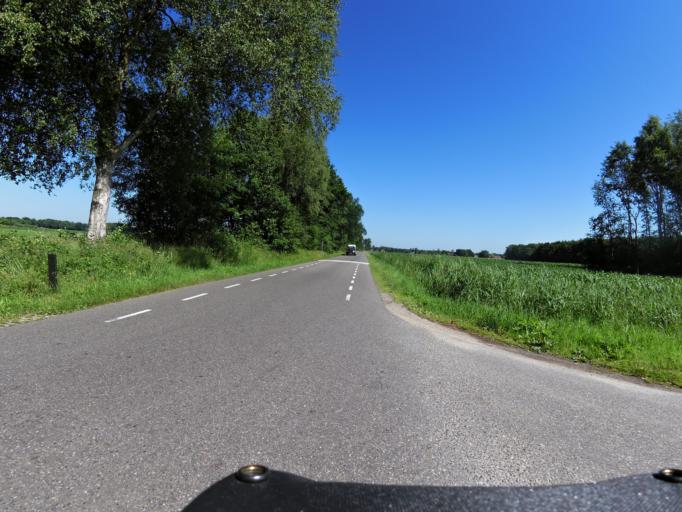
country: NL
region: Overijssel
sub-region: Gemeente Twenterand
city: Den Ham
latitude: 52.5294
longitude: 6.4456
